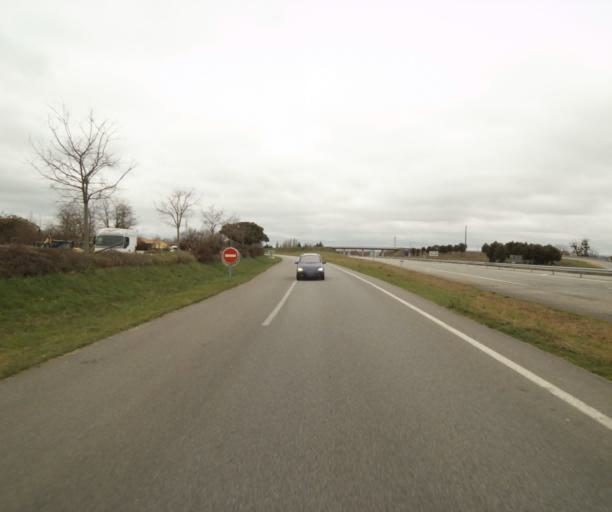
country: FR
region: Midi-Pyrenees
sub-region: Departement de l'Ariege
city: Pamiers
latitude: 43.1307
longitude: 1.6274
